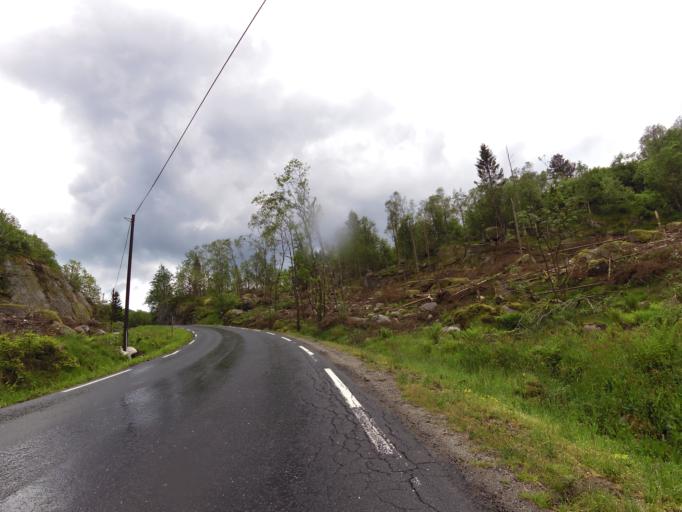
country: NO
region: Vest-Agder
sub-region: Lyngdal
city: Lyngdal
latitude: 58.1078
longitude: 7.0924
